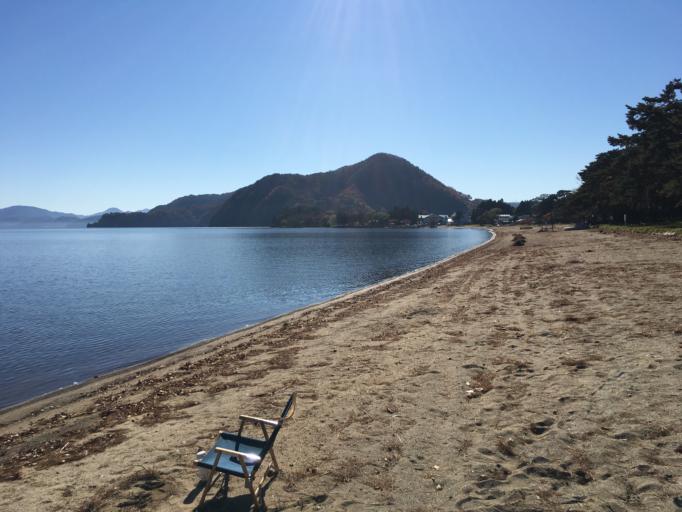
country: JP
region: Fukushima
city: Inawashiro
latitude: 37.4630
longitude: 140.0466
